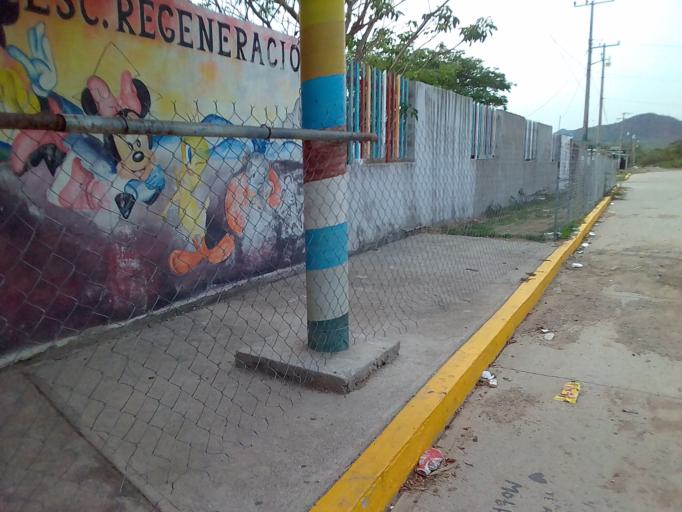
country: MX
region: Oaxaca
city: San Dionisio del Mar
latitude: 16.3268
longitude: -94.7583
